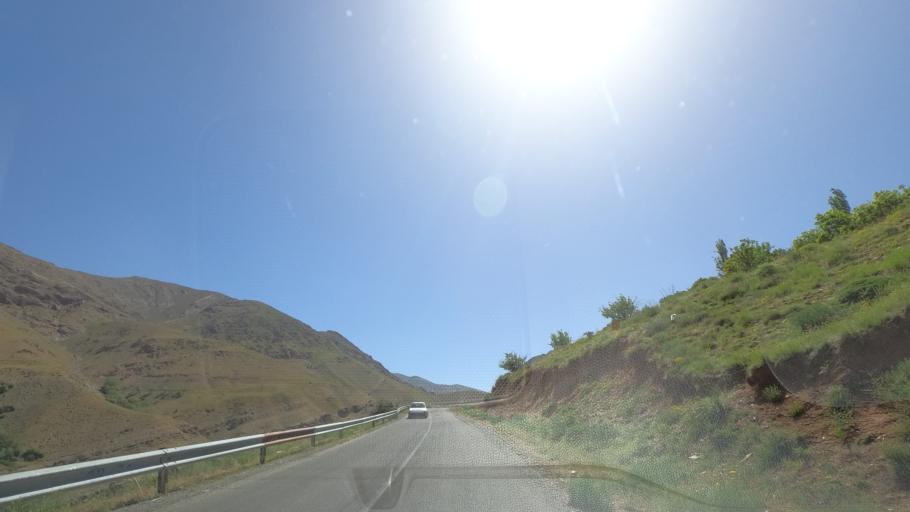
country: IR
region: Alborz
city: Karaj
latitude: 35.9235
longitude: 51.1585
